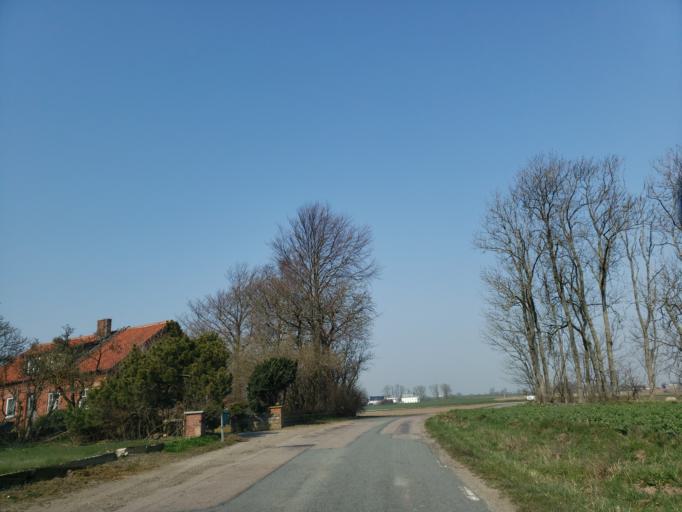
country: SE
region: Skane
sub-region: Simrishamns Kommun
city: Simrishamn
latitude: 55.4645
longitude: 14.2082
